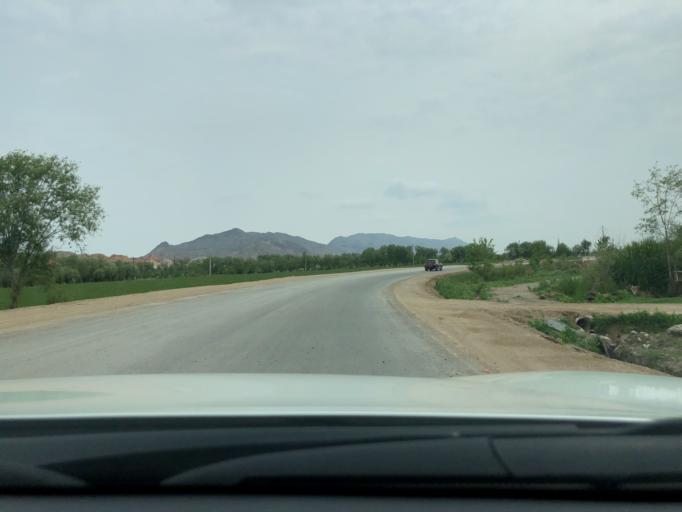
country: TJ
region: Viloyati Sughd
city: Isfara
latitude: 40.1519
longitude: 70.6194
